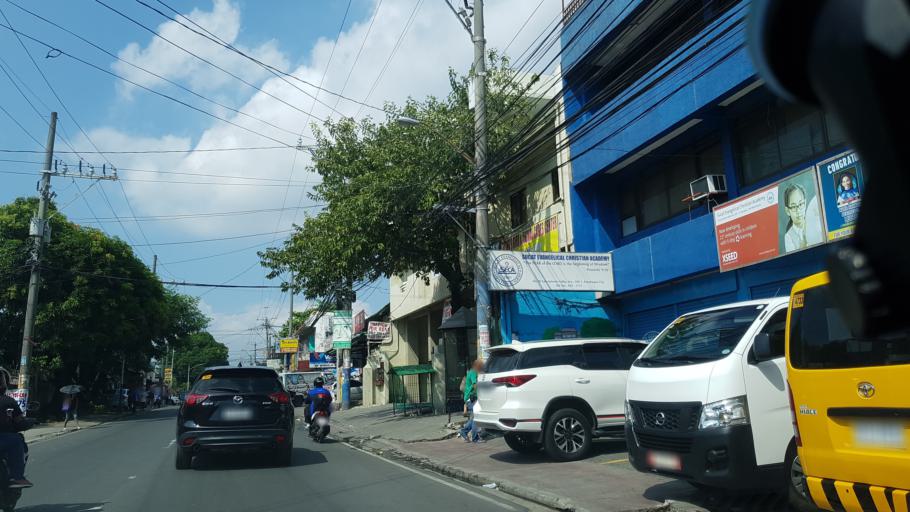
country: PH
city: Sambayanihan People's Village
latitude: 14.4678
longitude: 121.0209
